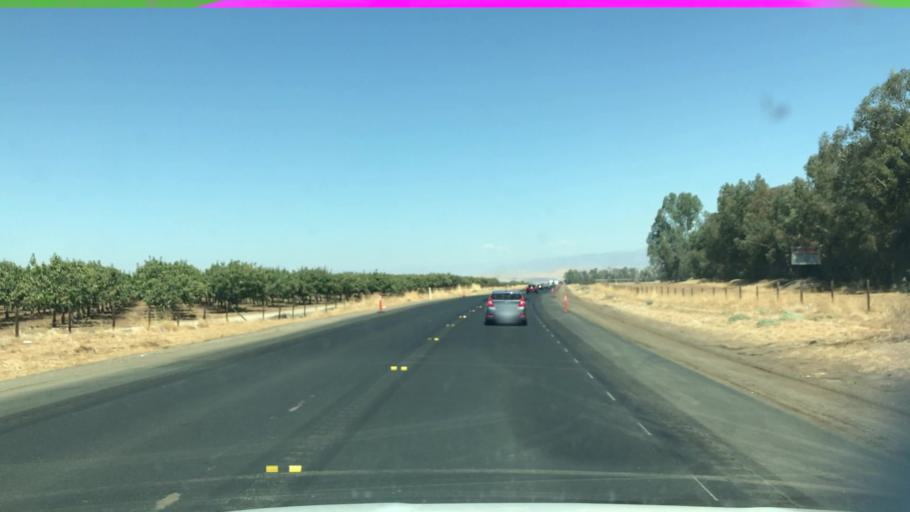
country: US
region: California
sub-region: Tulare County
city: Terra Bella
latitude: 35.9827
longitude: -119.0528
